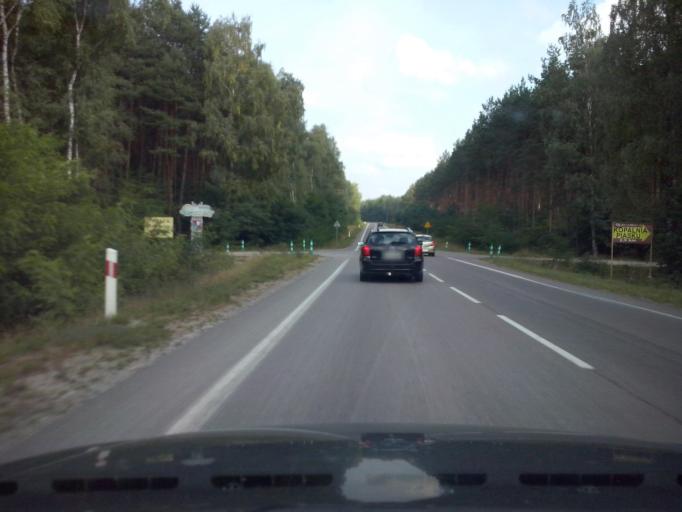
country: PL
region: Subcarpathian Voivodeship
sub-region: Powiat mielecki
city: Przeclaw
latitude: 50.2762
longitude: 21.5400
